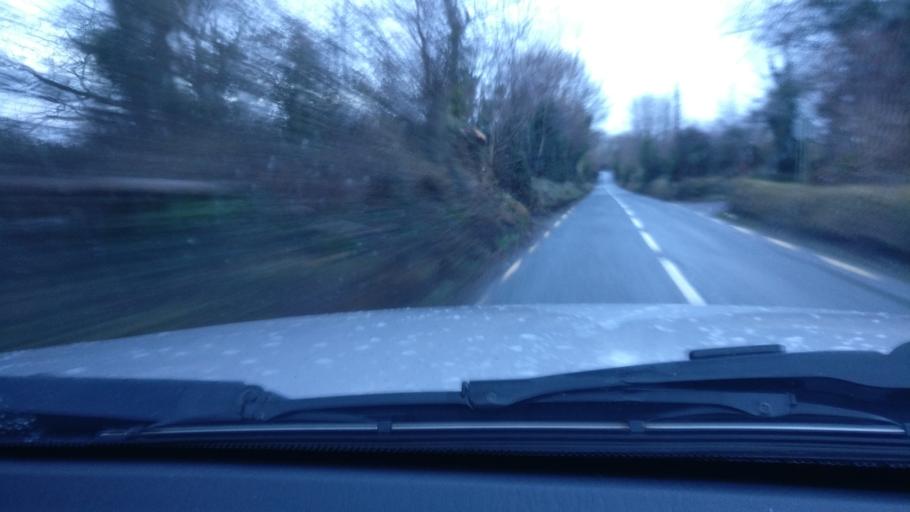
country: IE
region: Connaught
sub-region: County Galway
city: Ballinasloe
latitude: 53.2668
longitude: -8.2518
